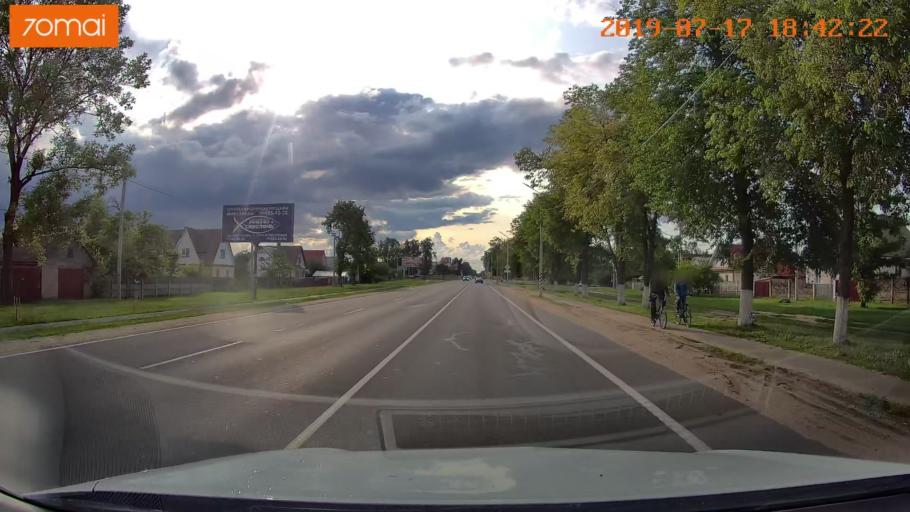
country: BY
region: Mogilev
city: Asipovichy
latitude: 53.3095
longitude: 28.6504
